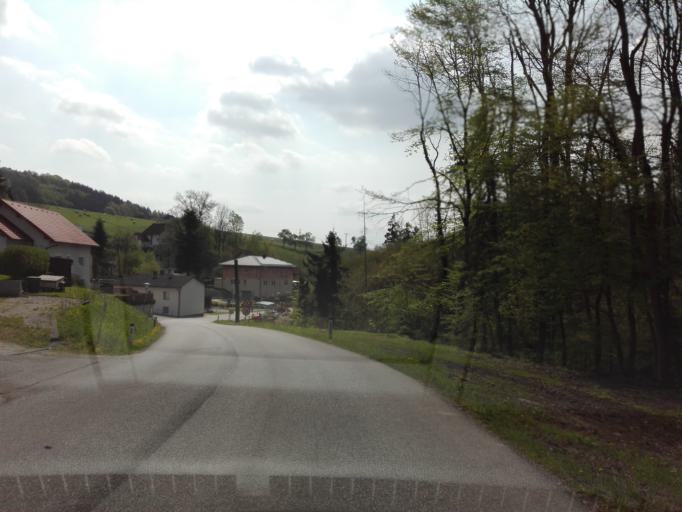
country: AT
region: Upper Austria
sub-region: Politischer Bezirk Perg
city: Perg
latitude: 48.2352
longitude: 14.7043
